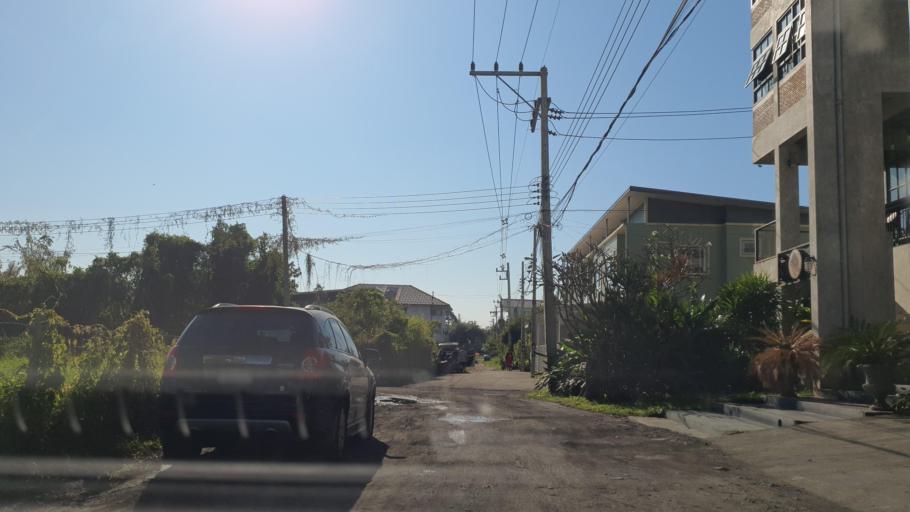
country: TH
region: Chiang Mai
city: Chiang Mai
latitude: 18.7731
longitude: 98.9479
